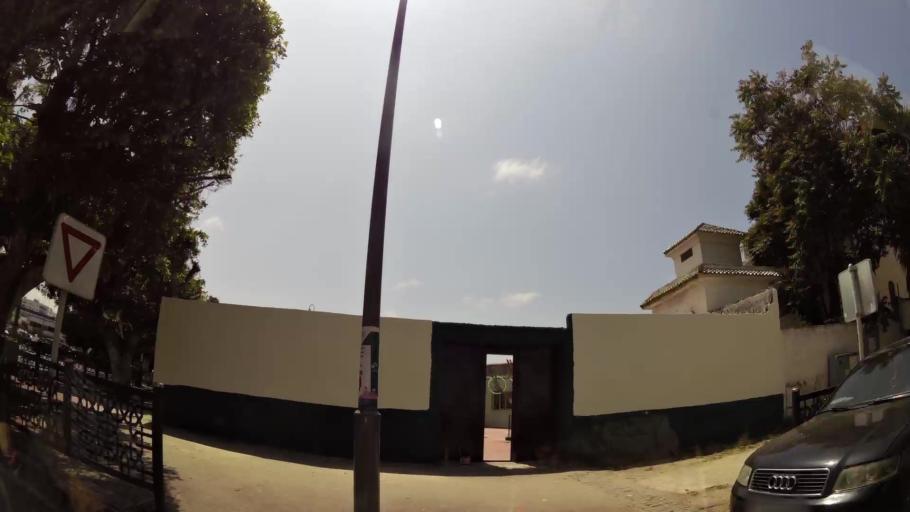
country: MA
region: Rabat-Sale-Zemmour-Zaer
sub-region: Rabat
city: Rabat
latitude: 34.0091
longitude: -6.8544
